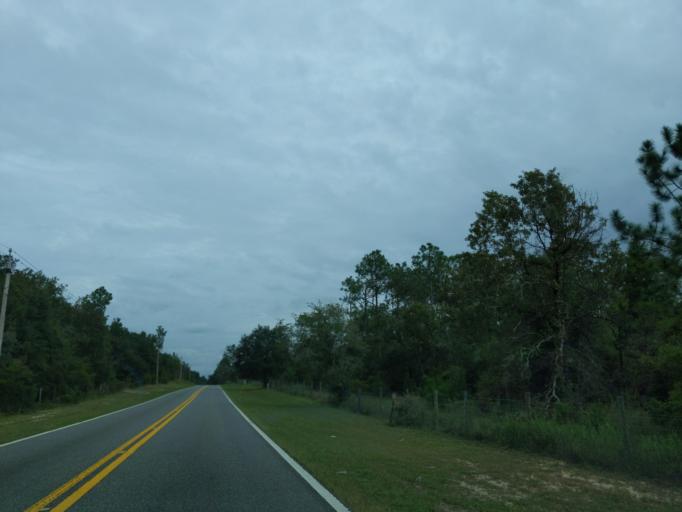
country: US
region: Florida
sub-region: Leon County
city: Woodville
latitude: 30.3742
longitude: -84.2075
